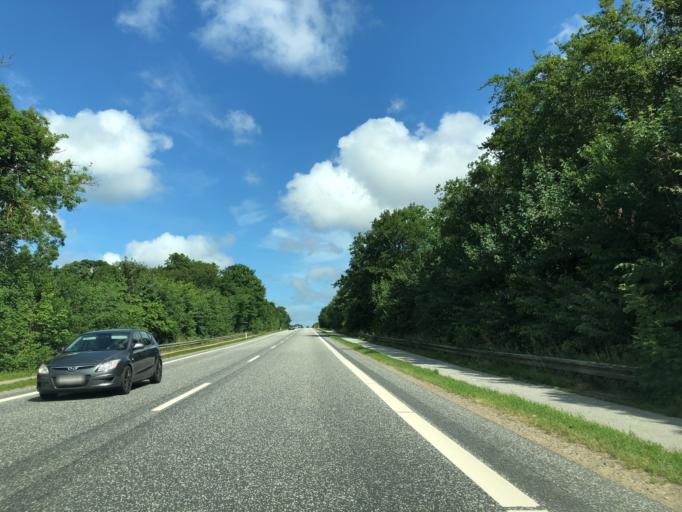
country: DK
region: Central Jutland
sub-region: Struer Kommune
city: Struer
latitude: 56.4582
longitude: 8.5907
